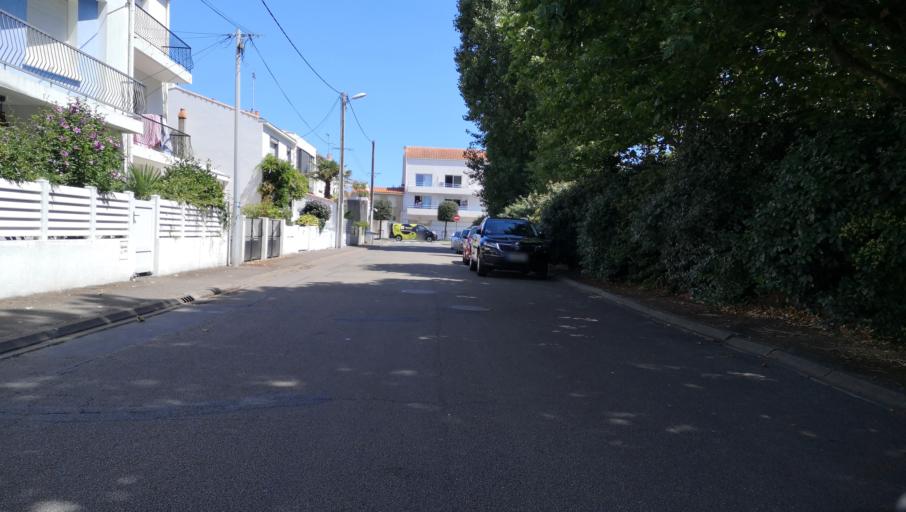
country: FR
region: Pays de la Loire
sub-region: Departement de la Vendee
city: Les Sables-d'Olonne
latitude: 46.4935
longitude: -1.7655
